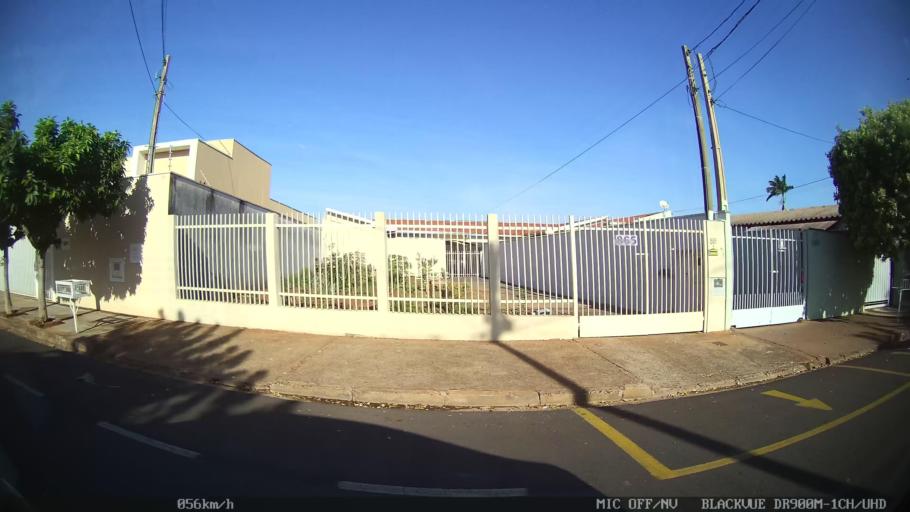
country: BR
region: Sao Paulo
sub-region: Sao Jose Do Rio Preto
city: Sao Jose do Rio Preto
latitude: -20.8176
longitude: -49.4052
